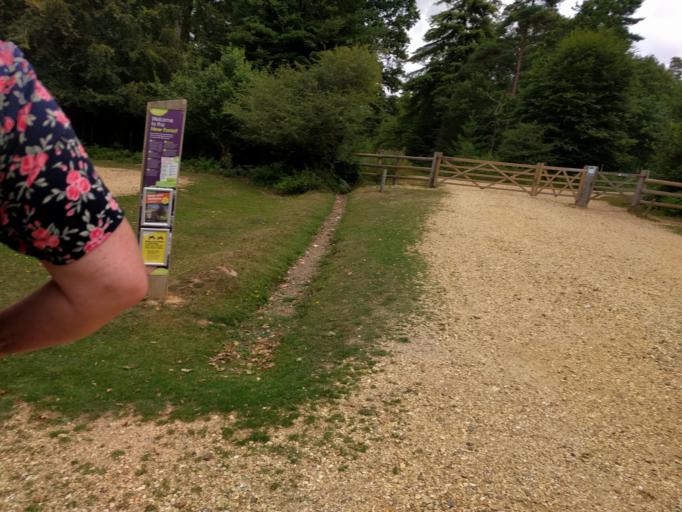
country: GB
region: England
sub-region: Hampshire
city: Brockenhurst
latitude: 50.8313
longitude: -1.5545
